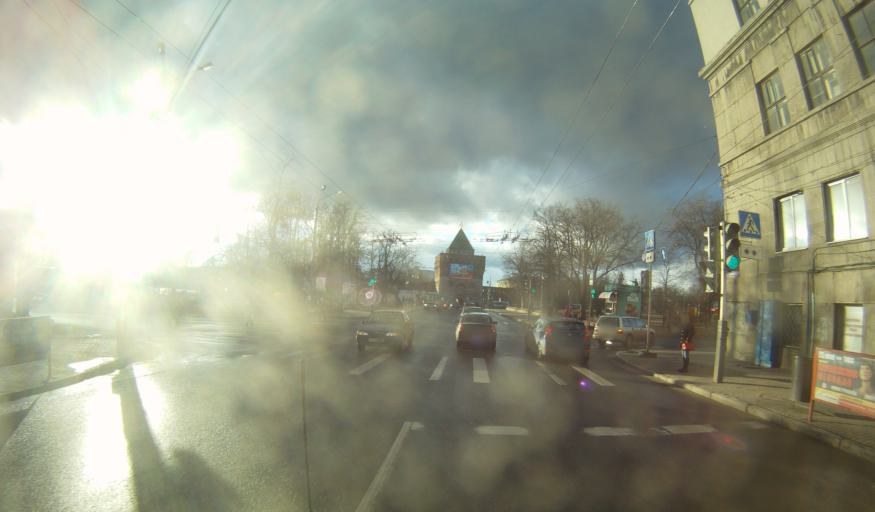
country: RU
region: Nizjnij Novgorod
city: Nizhniy Novgorod
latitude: 56.3256
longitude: 44.0072
